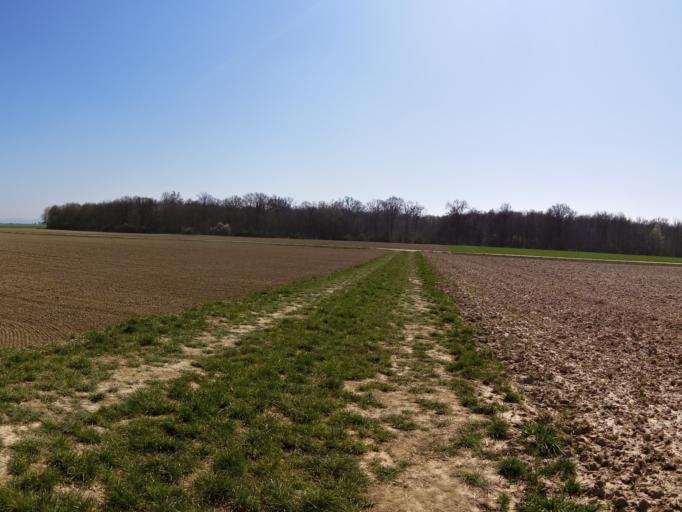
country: DE
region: Bavaria
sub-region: Regierungsbezirk Unterfranken
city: Kurnach
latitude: 49.8367
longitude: 10.0659
